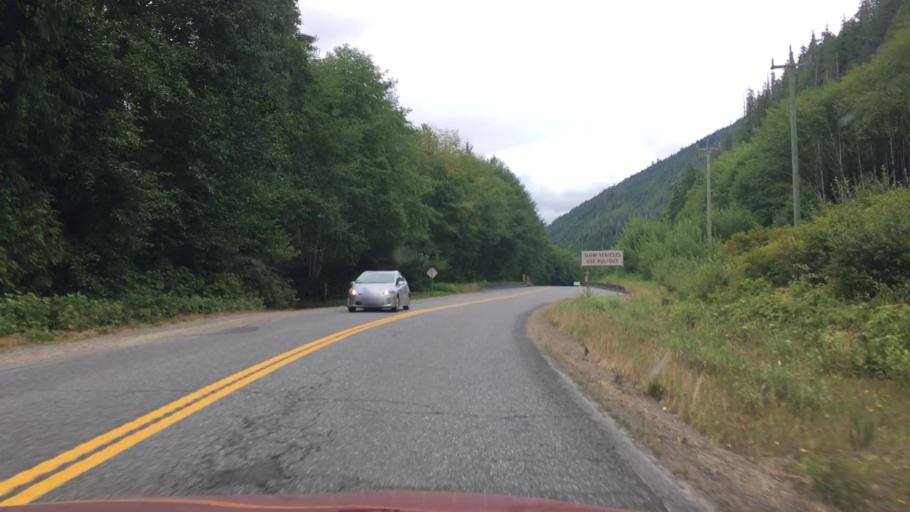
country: CA
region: British Columbia
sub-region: Regional District of Alberni-Clayoquot
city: Ucluelet
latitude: 49.0464
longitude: -125.5027
